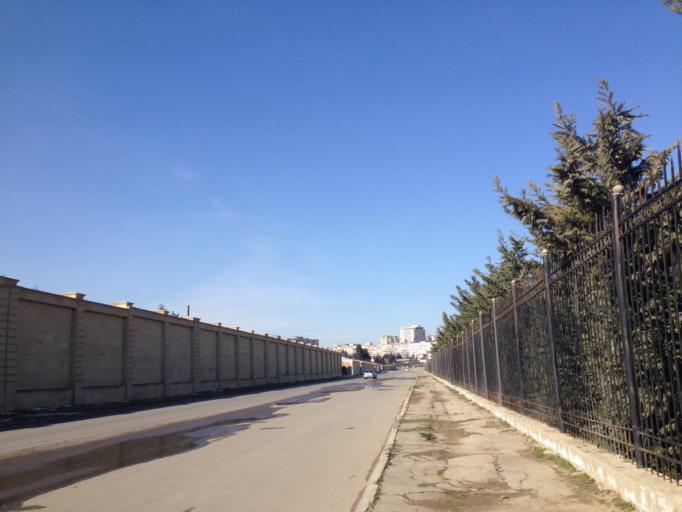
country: AZ
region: Baki
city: Baku
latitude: 40.4083
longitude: 49.8571
